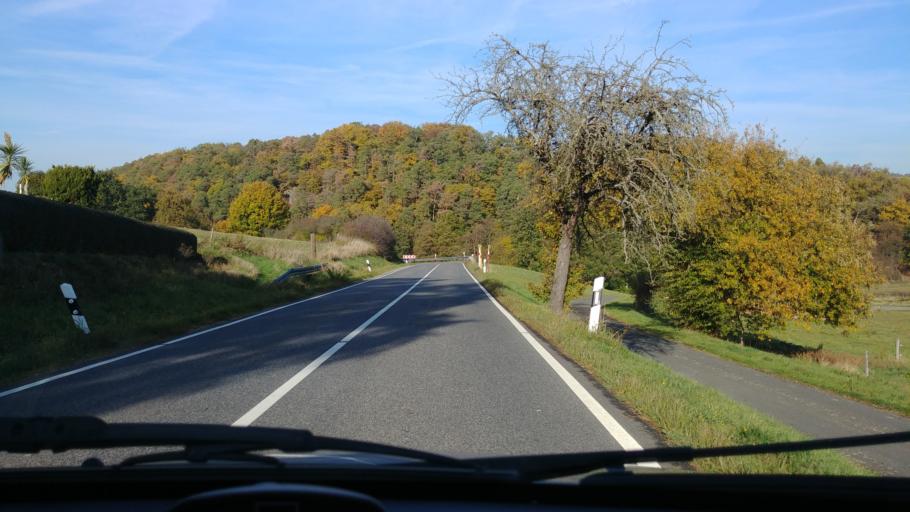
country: DE
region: Hesse
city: Burg Hohenstein
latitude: 50.2135
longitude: 8.0873
